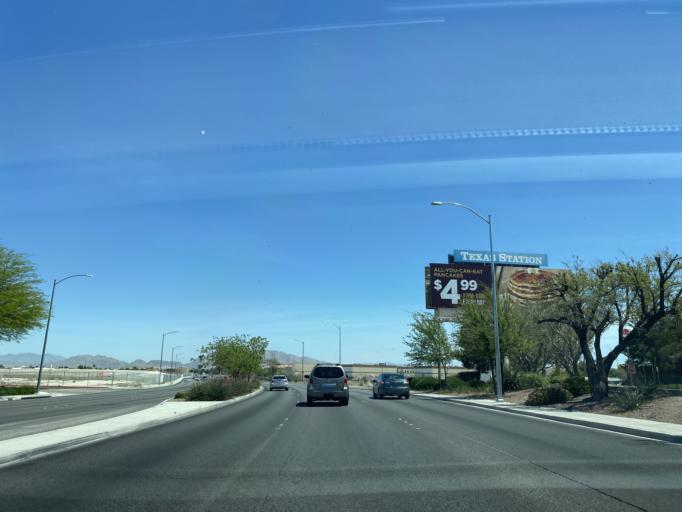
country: US
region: Nevada
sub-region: Clark County
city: Las Vegas
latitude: 36.1978
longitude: -115.1889
